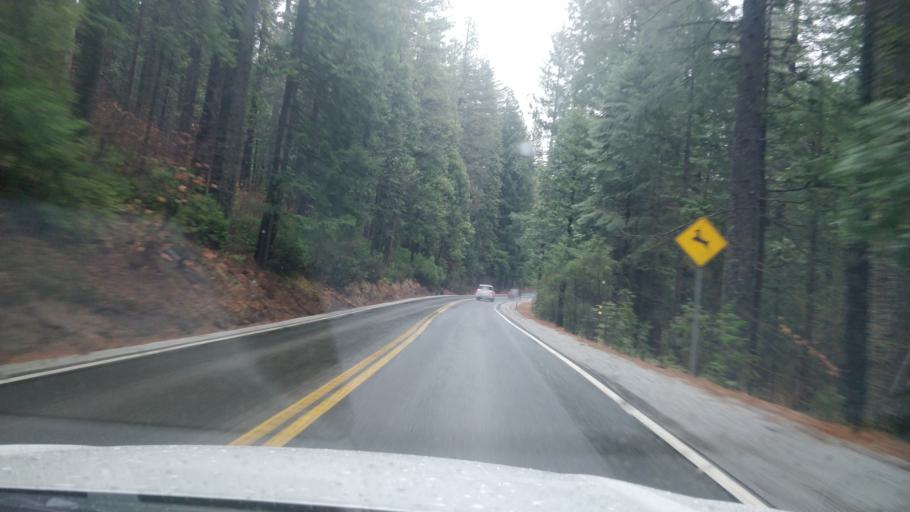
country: US
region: California
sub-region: Nevada County
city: Nevada City
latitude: 39.3157
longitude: -120.8017
